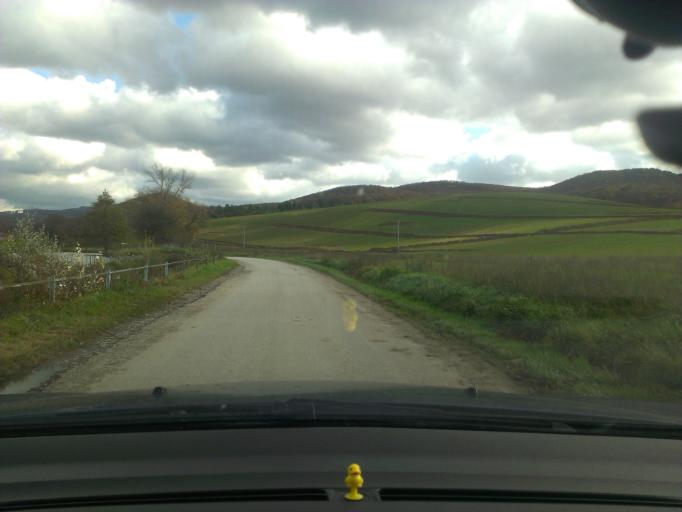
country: SK
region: Trnavsky
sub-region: Okres Trnava
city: Piestany
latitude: 48.6057
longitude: 17.8786
